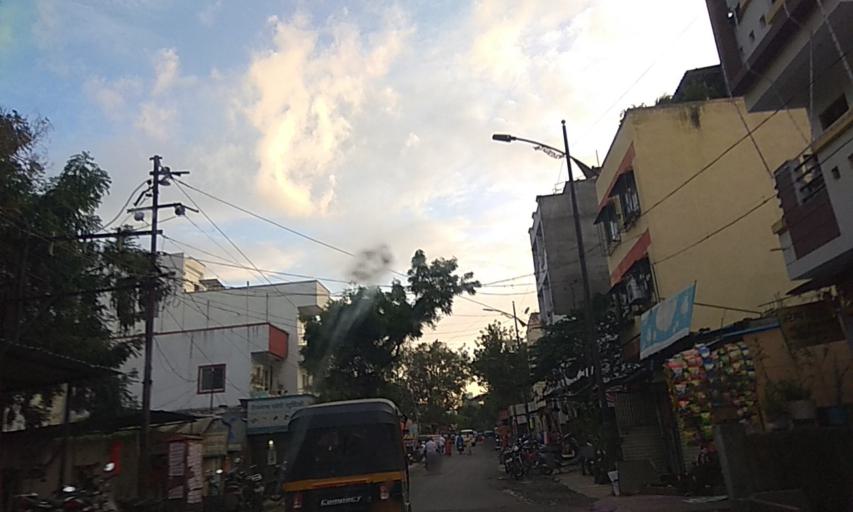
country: IN
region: Maharashtra
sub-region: Pune Division
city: Pune
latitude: 18.4951
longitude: 73.8510
